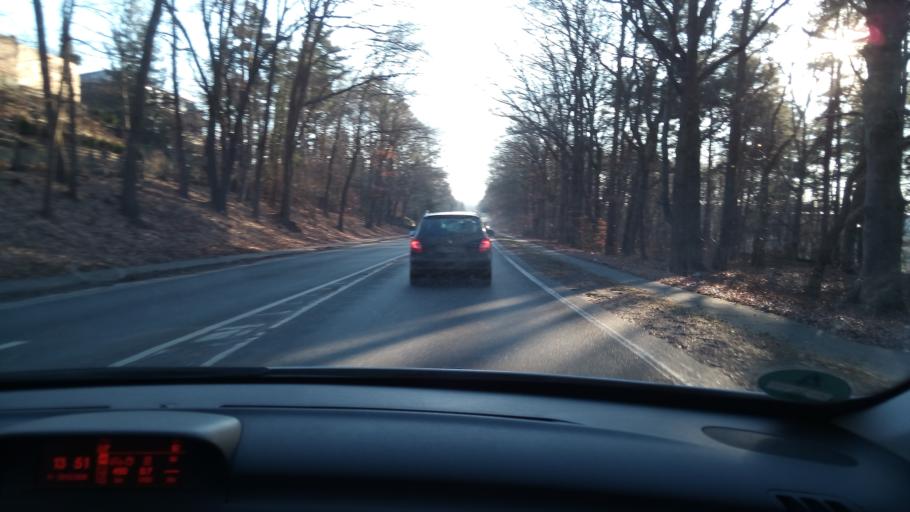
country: DE
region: Lower Saxony
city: Adendorf
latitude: 53.2781
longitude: 10.4275
